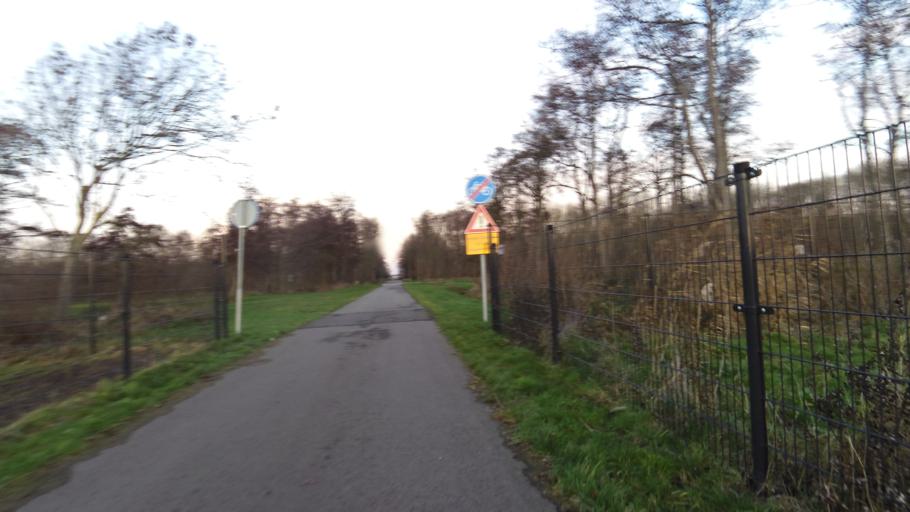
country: NL
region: South Holland
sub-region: Gemeente Noordwijkerhout
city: Noordwijkerhout
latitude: 52.2748
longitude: 4.4848
